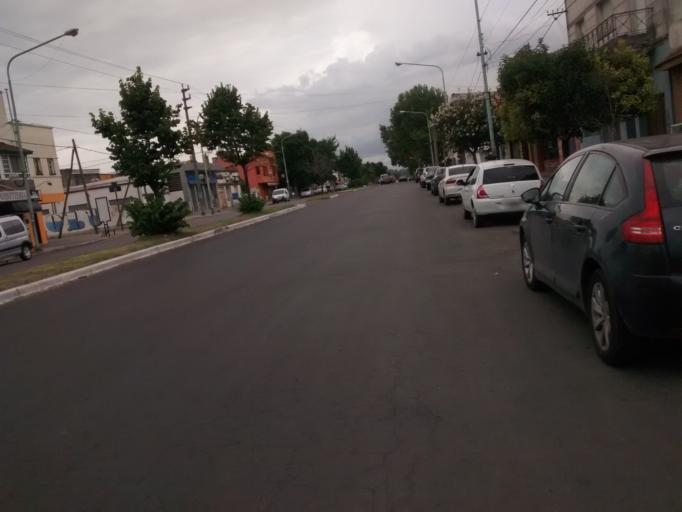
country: AR
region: Buenos Aires
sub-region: Partido de La Plata
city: La Plata
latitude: -34.9361
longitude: -57.9212
